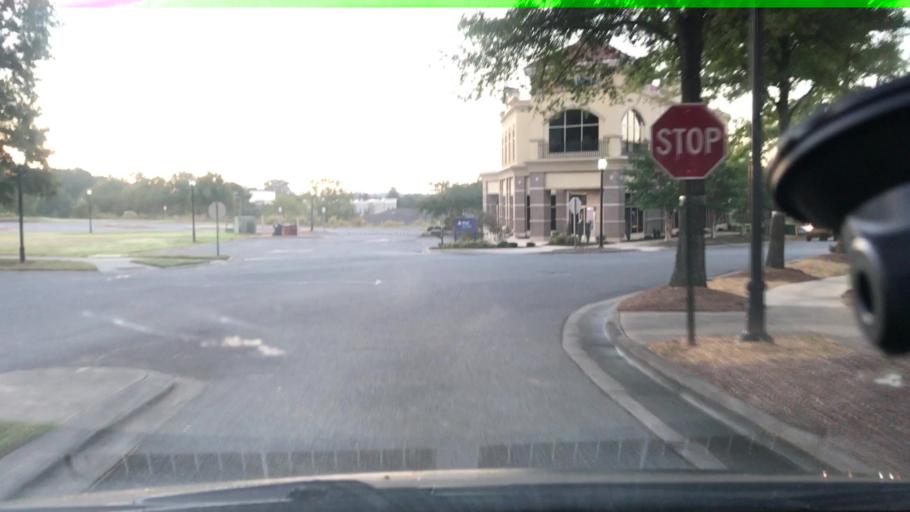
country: US
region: North Carolina
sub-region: Mecklenburg County
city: Cornelius
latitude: 35.4477
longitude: -80.8914
